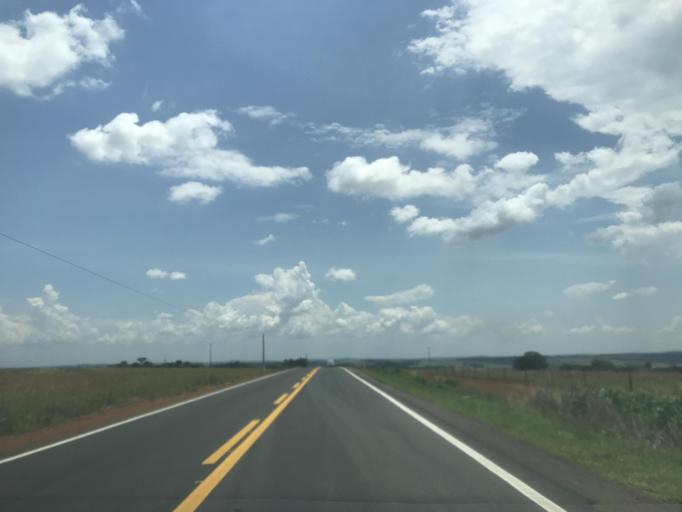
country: BR
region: Goias
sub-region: Bela Vista De Goias
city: Bela Vista de Goias
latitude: -17.0990
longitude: -48.6596
